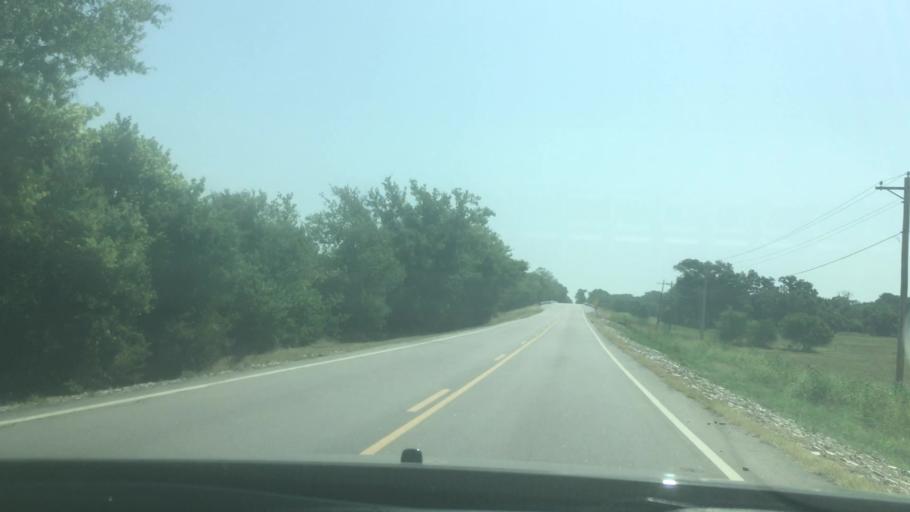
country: US
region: Oklahoma
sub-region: Bryan County
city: Durant
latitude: 34.1427
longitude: -96.4055
